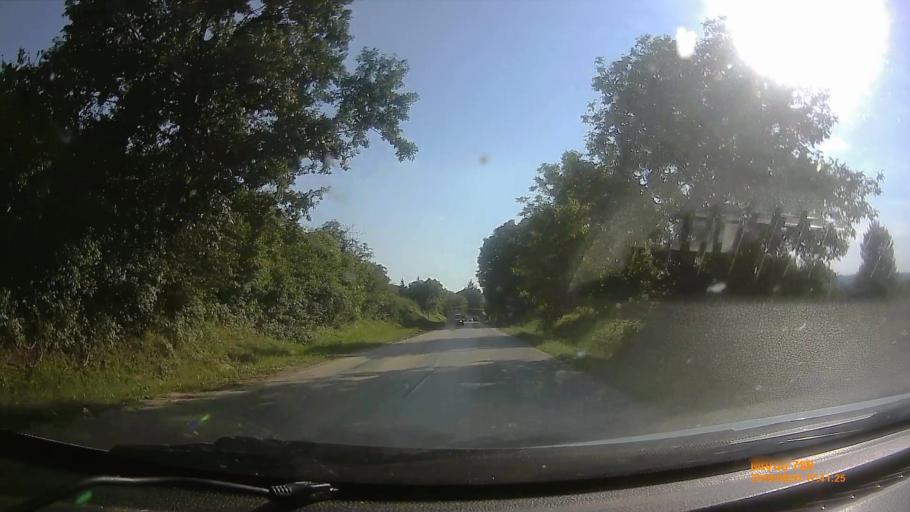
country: HU
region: Baranya
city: Komlo
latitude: 46.1923
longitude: 18.1745
